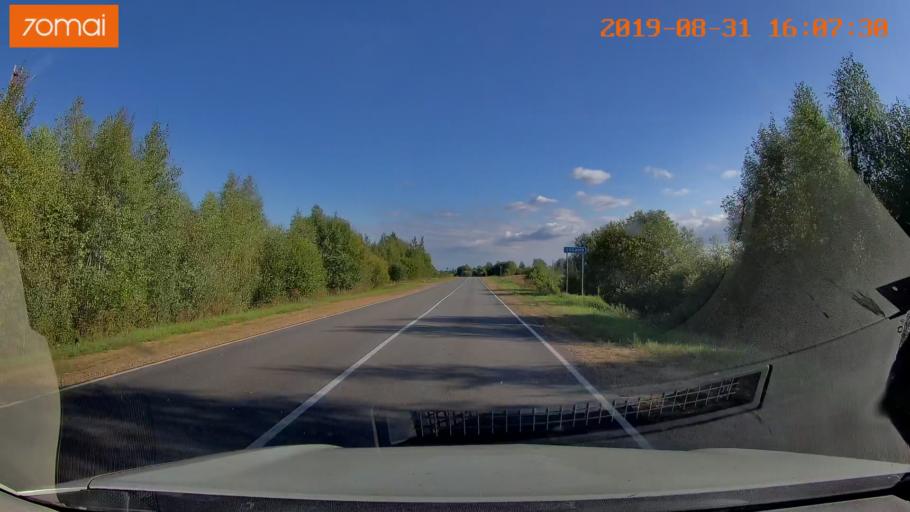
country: RU
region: Kaluga
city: Yukhnov
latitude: 54.6086
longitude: 35.3595
